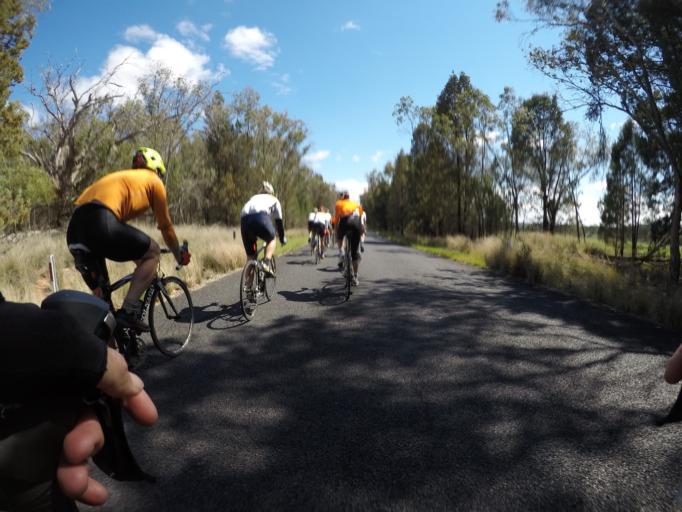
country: AU
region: New South Wales
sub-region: Dubbo Municipality
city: Dubbo
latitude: -32.5878
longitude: 148.5371
